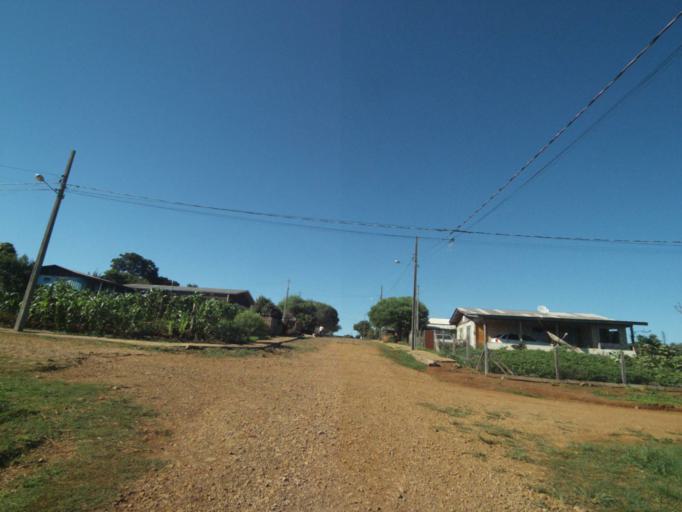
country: BR
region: Parana
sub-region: Pinhao
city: Pinhao
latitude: -25.8413
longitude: -52.0321
